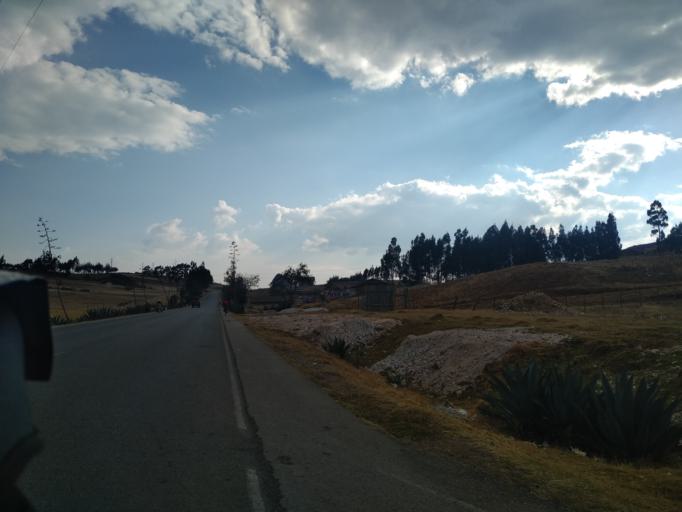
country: PE
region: Cajamarca
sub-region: Provincia de Cajamarca
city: Llacanora
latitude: -7.1433
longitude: -78.3923
